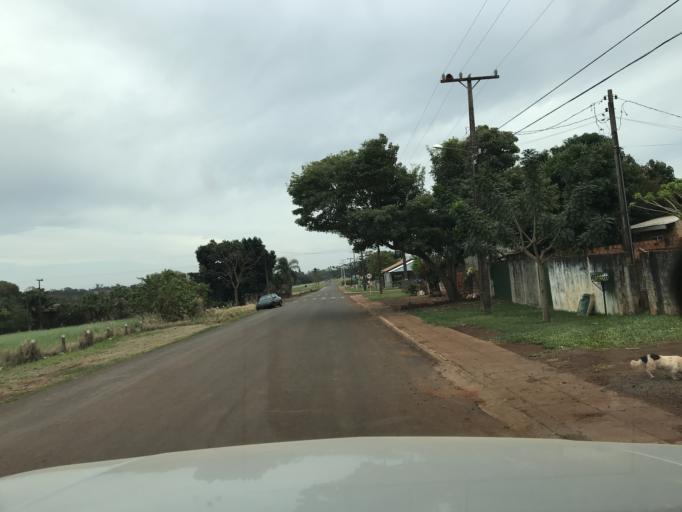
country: BR
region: Parana
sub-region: Marechal Candido Rondon
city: Marechal Candido Rondon
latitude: -24.4669
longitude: -53.9611
